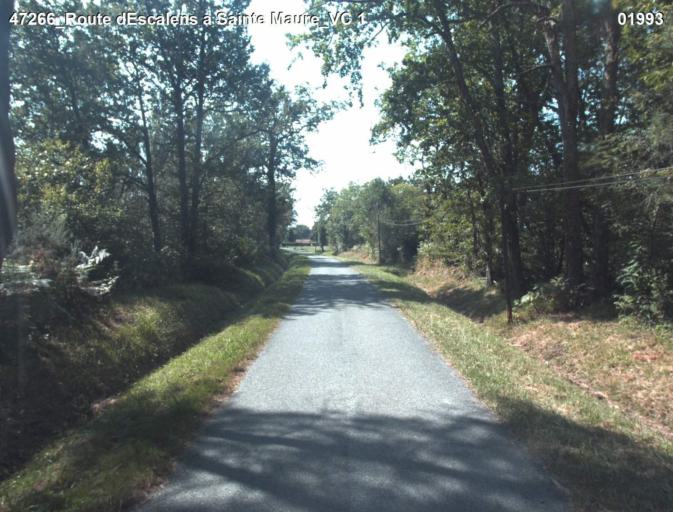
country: FR
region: Aquitaine
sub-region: Departement des Landes
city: Gabarret
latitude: 44.0086
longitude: 0.0806
